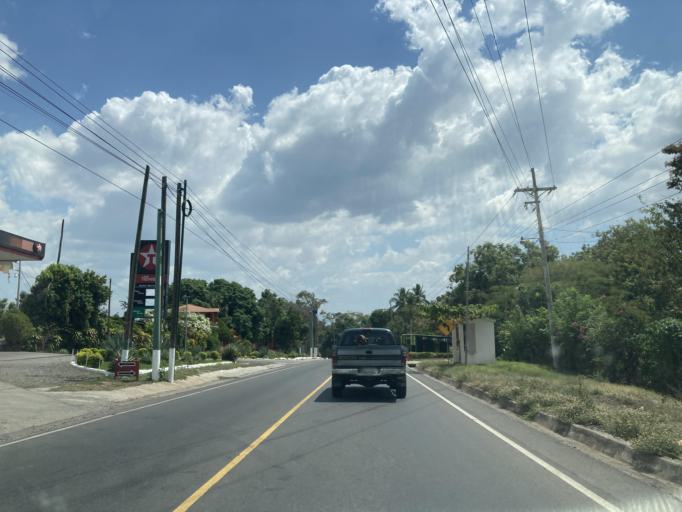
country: GT
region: Santa Rosa
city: Guazacapan
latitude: 14.0670
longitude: -90.4101
